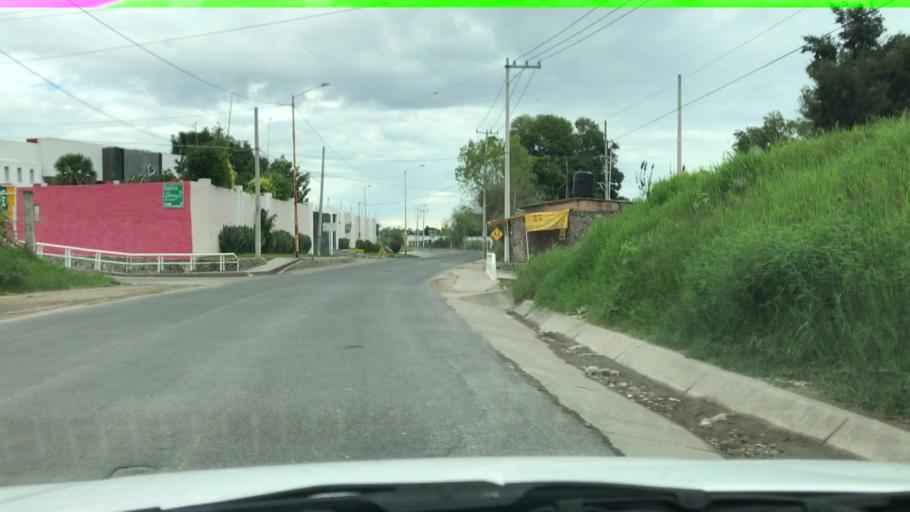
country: MX
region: Jalisco
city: Nicolas R Casillas
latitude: 20.5469
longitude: -103.4795
